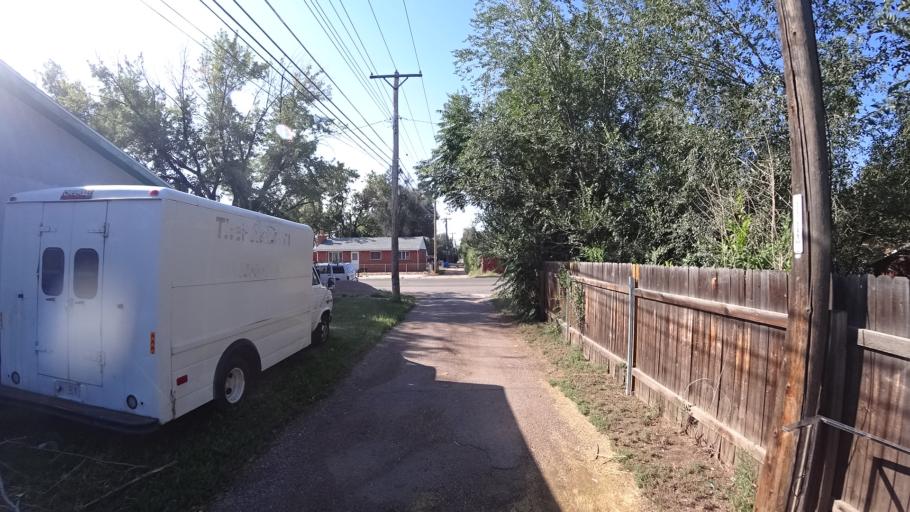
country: US
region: Colorado
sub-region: El Paso County
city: Colorado Springs
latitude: 38.8737
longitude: -104.8263
